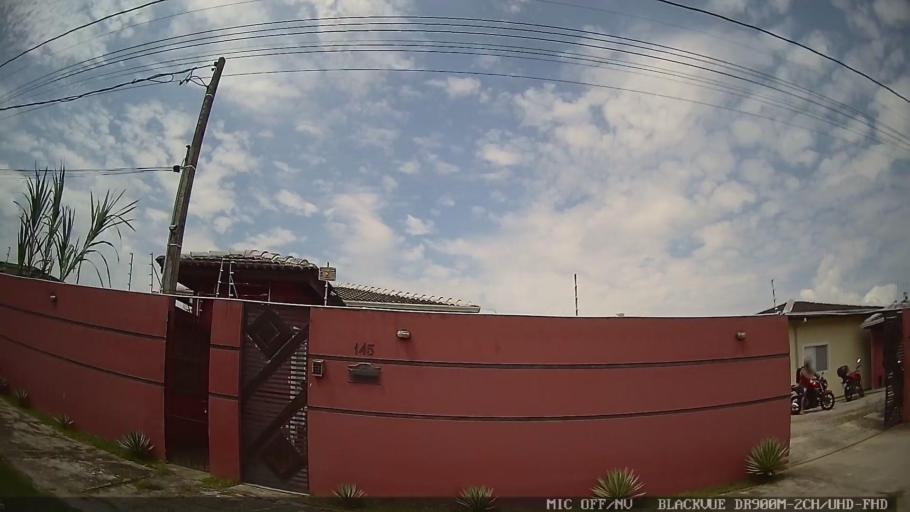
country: BR
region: Sao Paulo
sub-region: Caraguatatuba
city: Caraguatatuba
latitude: -23.6687
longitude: -45.4540
